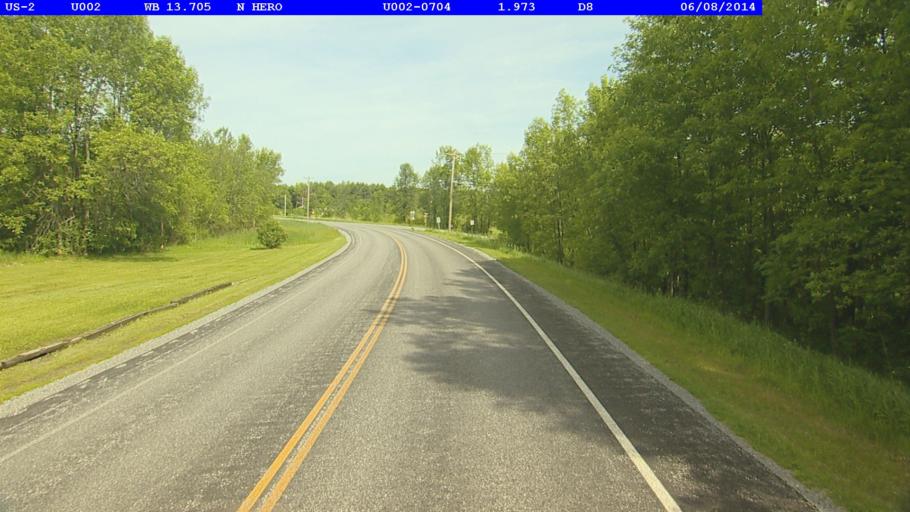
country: US
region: Vermont
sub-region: Grand Isle County
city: North Hero
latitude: 44.8615
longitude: -73.2594
